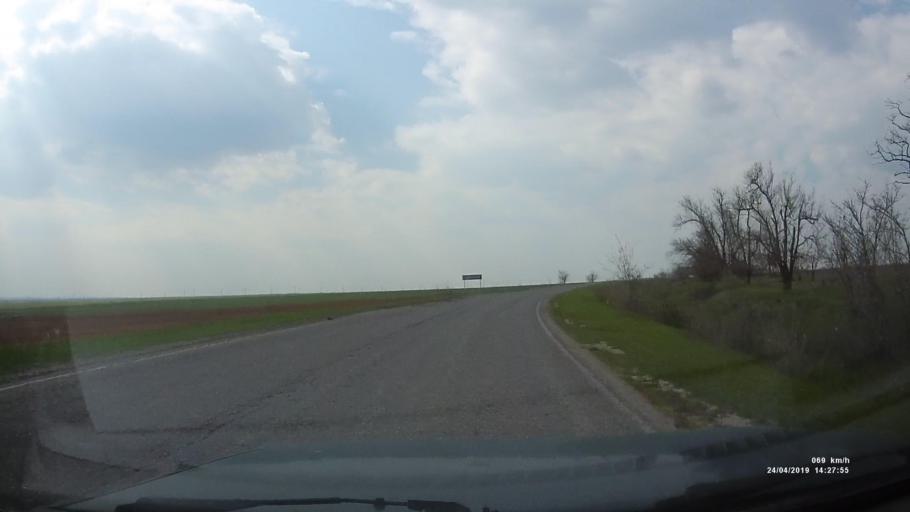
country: RU
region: Kalmykiya
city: Arshan'
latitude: 46.3345
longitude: 44.0349
